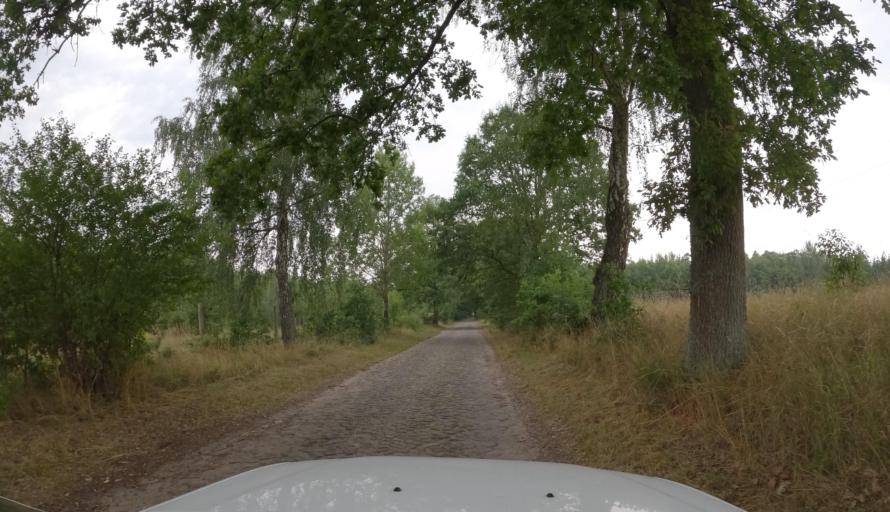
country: PL
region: West Pomeranian Voivodeship
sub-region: Powiat kolobrzeski
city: Ryman
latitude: 53.8551
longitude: 15.5827
